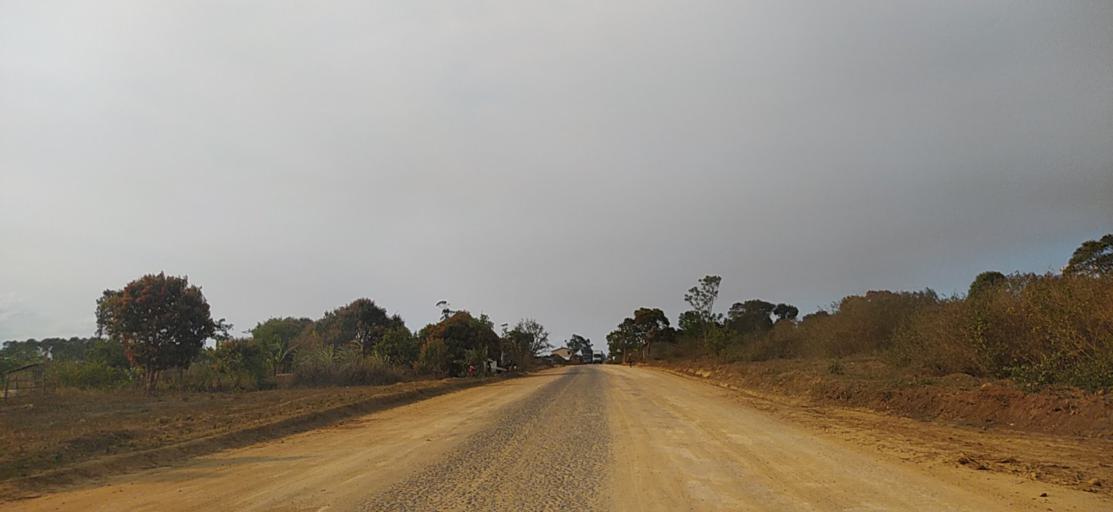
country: MG
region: Alaotra Mangoro
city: Moramanga
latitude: -18.6380
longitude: 48.2758
